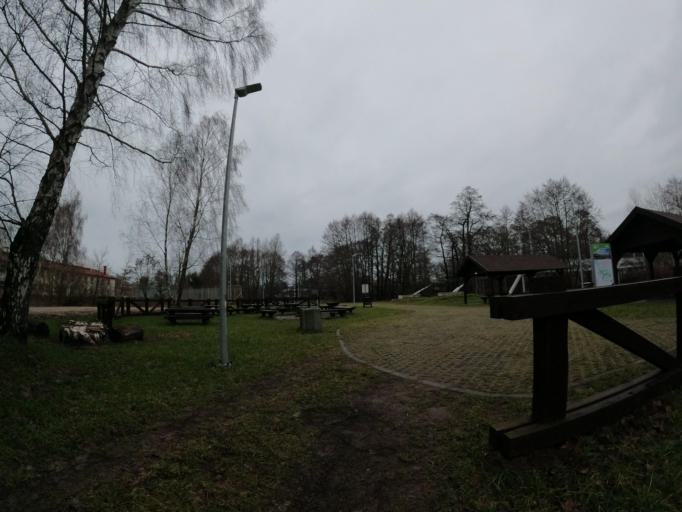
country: PL
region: Pomeranian Voivodeship
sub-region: Powiat slupski
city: Ustka
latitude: 54.5769
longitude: 16.8619
